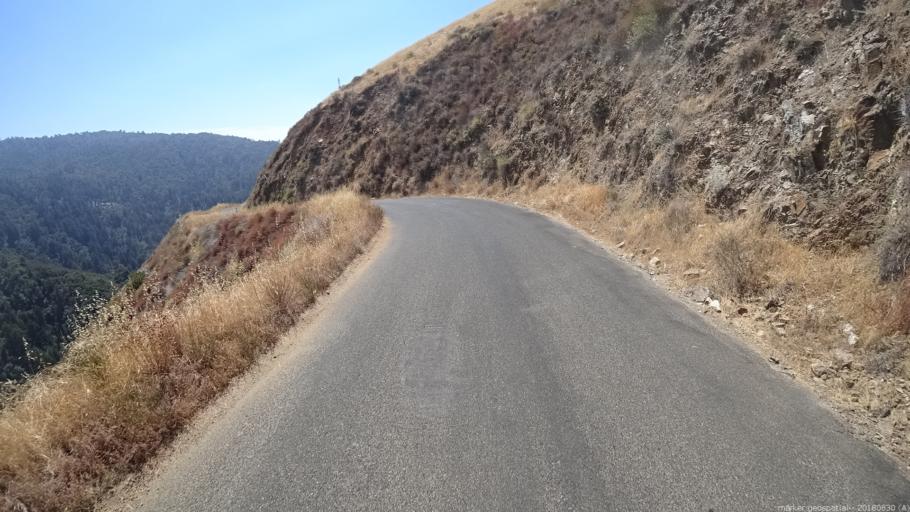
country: US
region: California
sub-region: Monterey County
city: Greenfield
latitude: 35.9984
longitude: -121.4577
